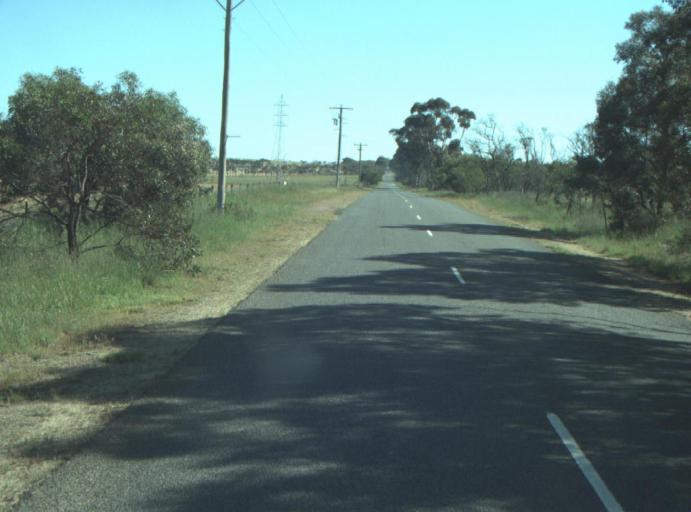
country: AU
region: Victoria
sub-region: Greater Geelong
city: Lara
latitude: -37.9341
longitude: 144.3939
